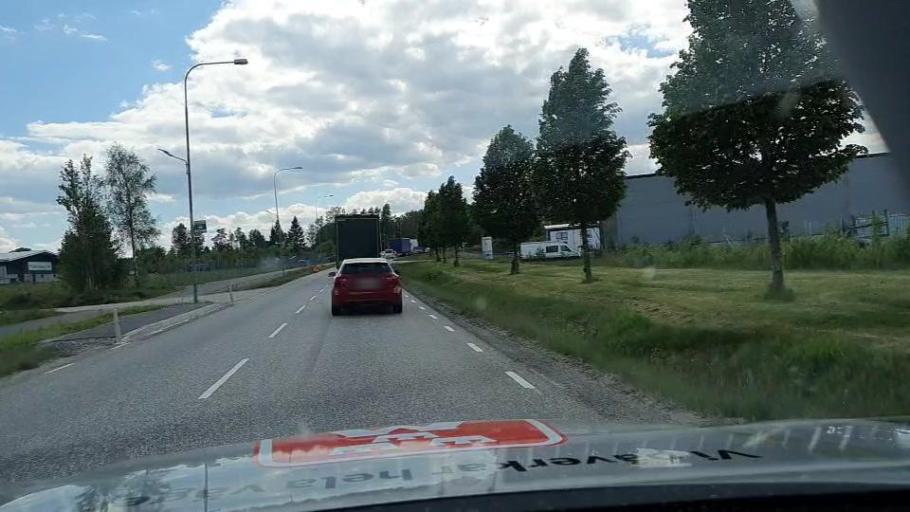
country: SE
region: Kronoberg
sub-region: Ljungby Kommun
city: Ljungby
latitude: 56.8450
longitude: 13.9200
